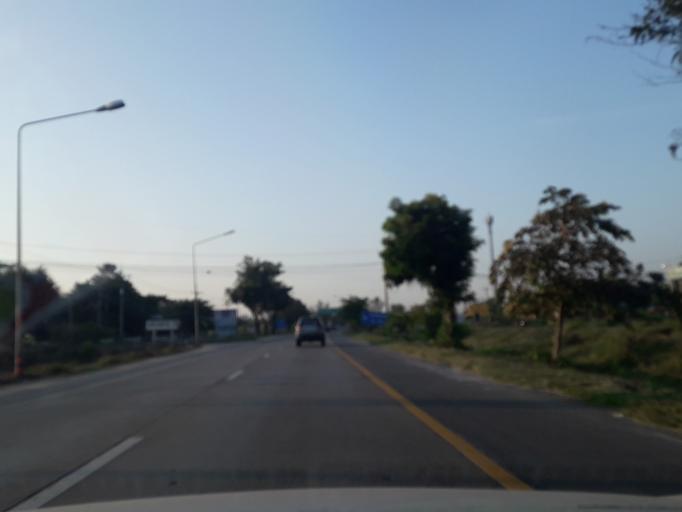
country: TH
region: Phra Nakhon Si Ayutthaya
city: Phra Nakhon Si Ayutthaya
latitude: 14.3188
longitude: 100.5277
